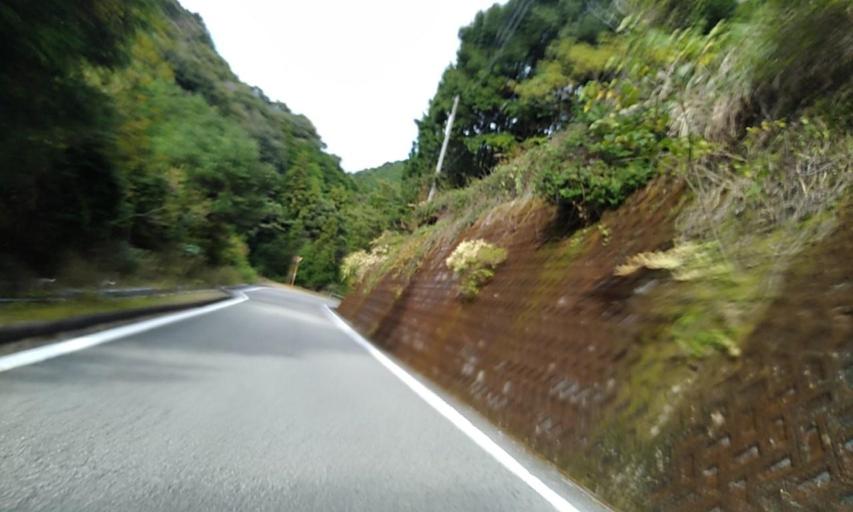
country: JP
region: Wakayama
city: Shingu
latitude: 33.5448
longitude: 135.8478
